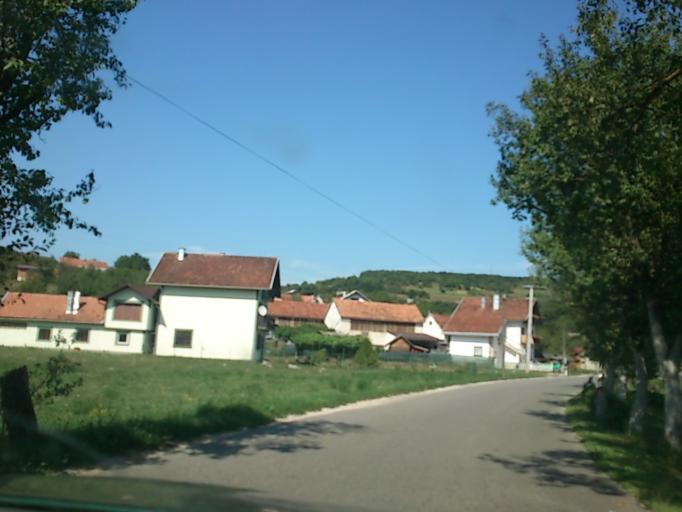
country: HR
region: Licko-Senjska
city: Otocac
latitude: 44.8737
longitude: 15.1784
